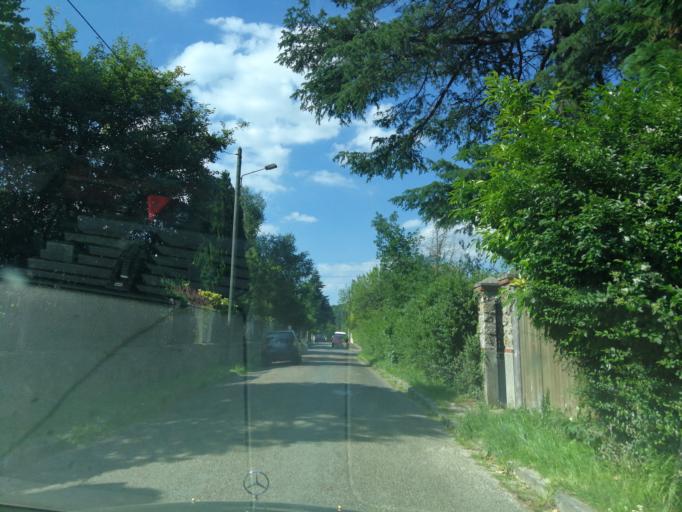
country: FR
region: Ile-de-France
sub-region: Departement des Yvelines
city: Saint-Remy-les-Chevreuse
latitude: 48.7140
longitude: 2.0656
